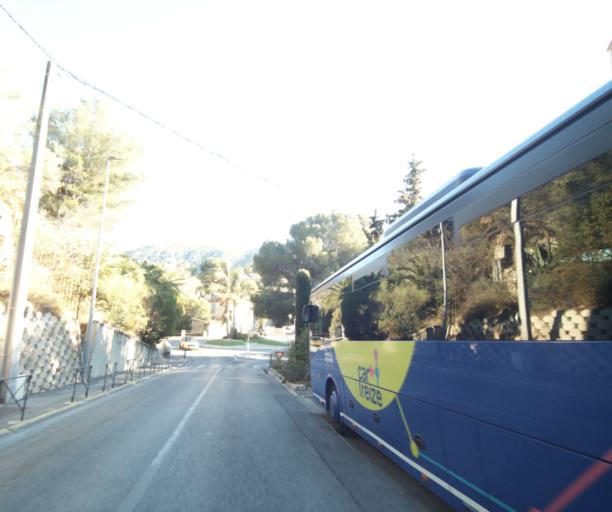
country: FR
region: Provence-Alpes-Cote d'Azur
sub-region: Departement des Bouches-du-Rhone
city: Cassis
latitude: 43.2156
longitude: 5.5434
